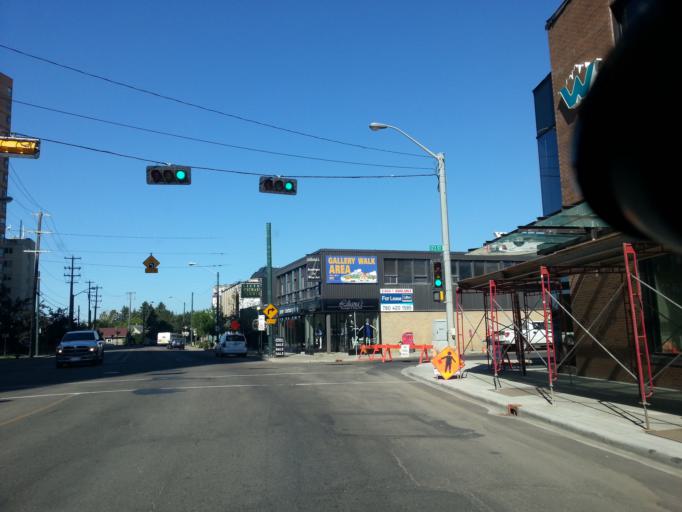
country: CA
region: Alberta
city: Edmonton
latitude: 53.5414
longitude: -113.5337
